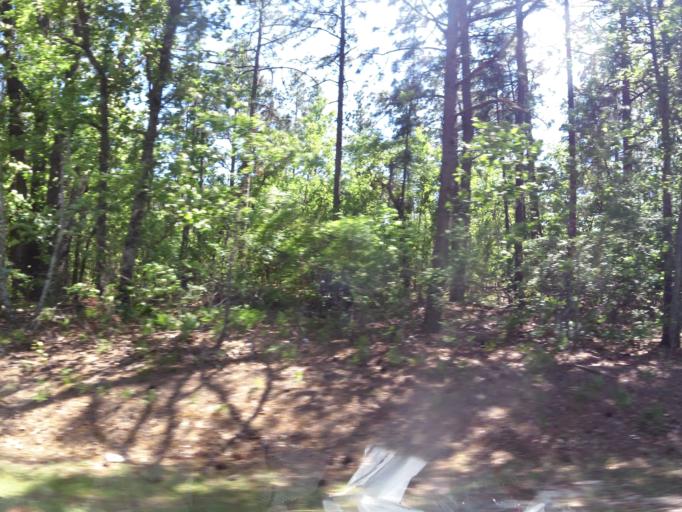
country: US
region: South Carolina
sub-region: Aiken County
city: New Ellenton
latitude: 33.5126
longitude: -81.5681
